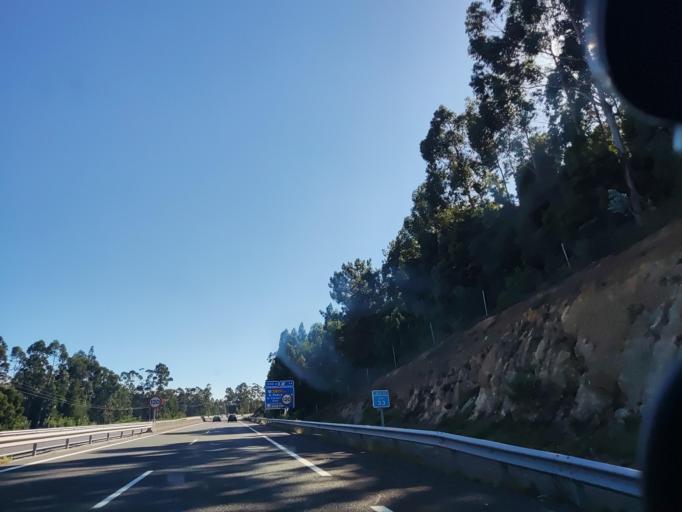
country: ES
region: Galicia
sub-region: Provincia da Coruna
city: Boiro
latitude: 42.6171
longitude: -8.9526
